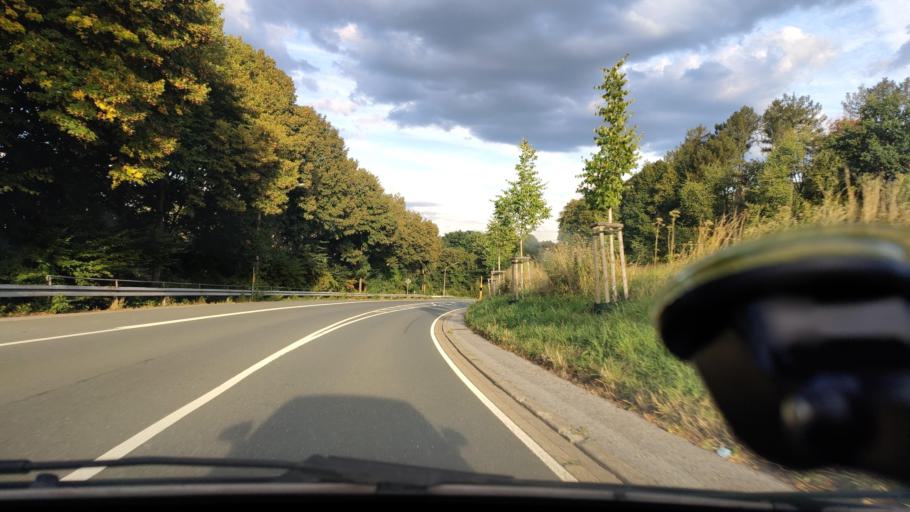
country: DE
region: North Rhine-Westphalia
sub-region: Regierungsbezirk Arnsberg
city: Nachrodt-Wiblingwerde
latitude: 51.3771
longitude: 7.6009
